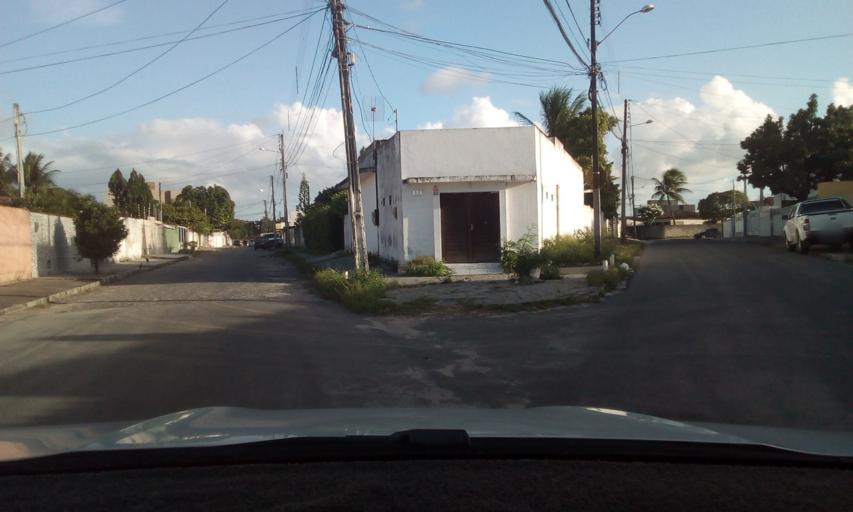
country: BR
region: Paraiba
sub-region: Joao Pessoa
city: Joao Pessoa
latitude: -7.1813
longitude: -34.8369
